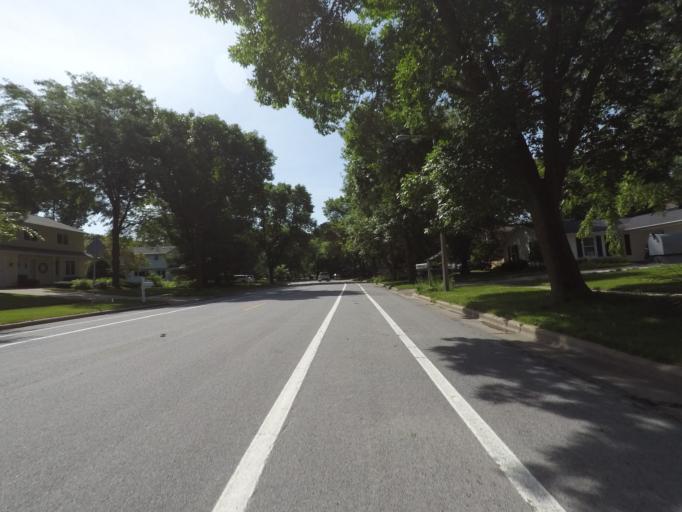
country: US
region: Wisconsin
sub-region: Dane County
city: Middleton
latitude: 43.0794
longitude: -89.5094
